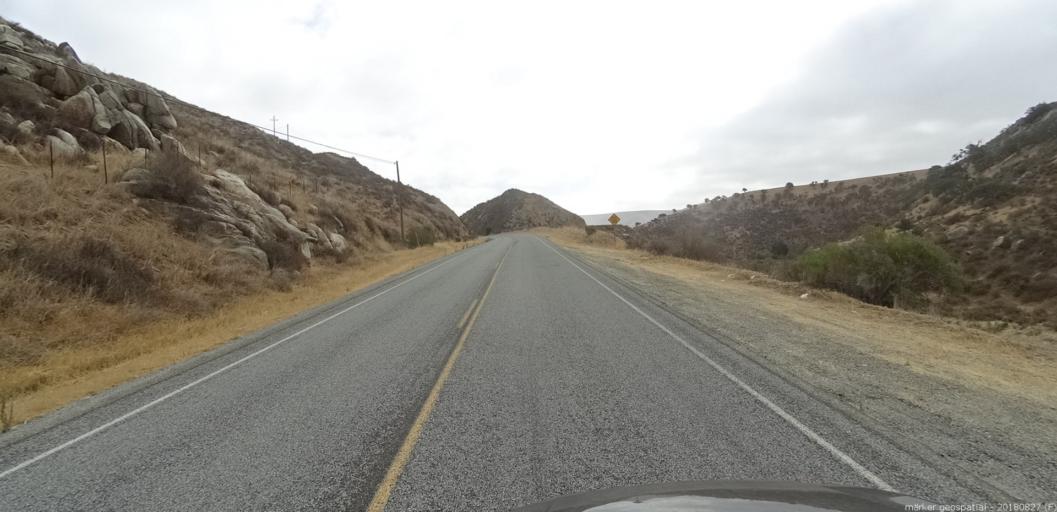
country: US
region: California
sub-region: Monterey County
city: King City
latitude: 36.2680
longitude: -121.0704
